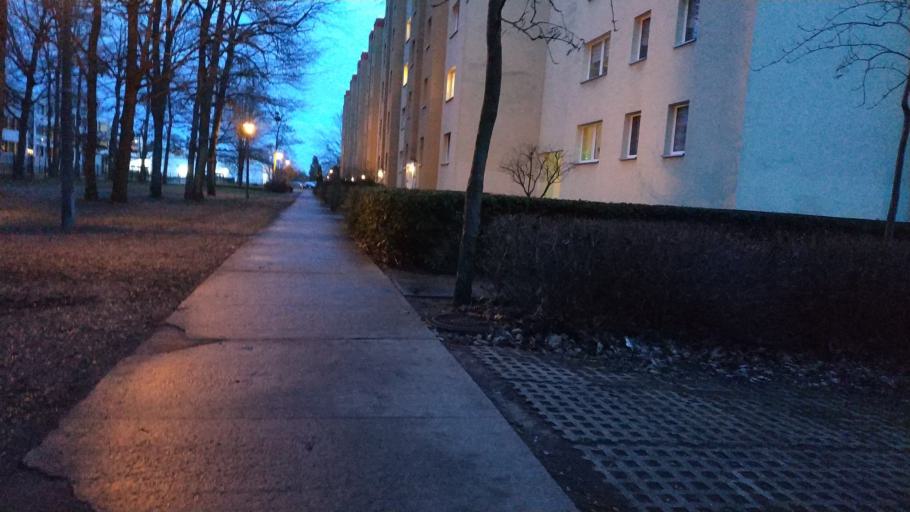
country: DE
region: Brandenburg
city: Petershagen
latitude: 52.5365
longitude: 13.8295
